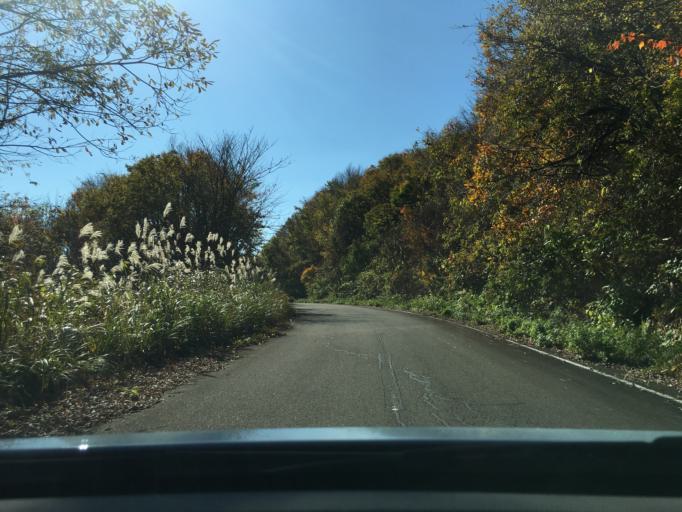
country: JP
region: Fukushima
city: Inawashiro
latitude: 37.4033
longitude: 140.0241
